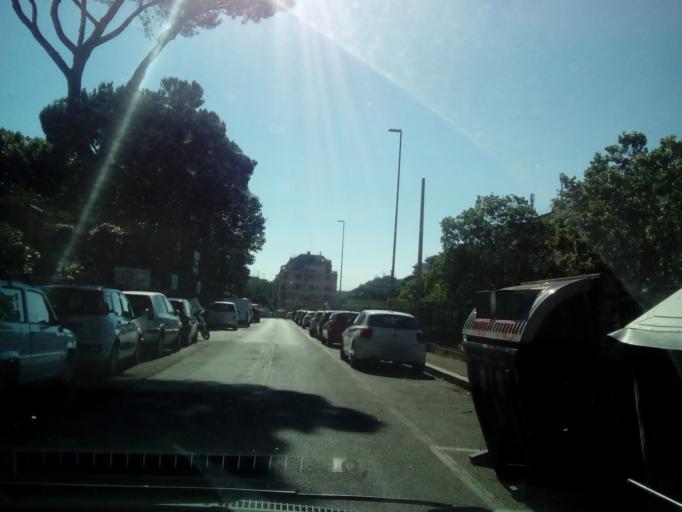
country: IT
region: Latium
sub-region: Citta metropolitana di Roma Capitale
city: Rome
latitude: 41.8948
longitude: 12.5677
